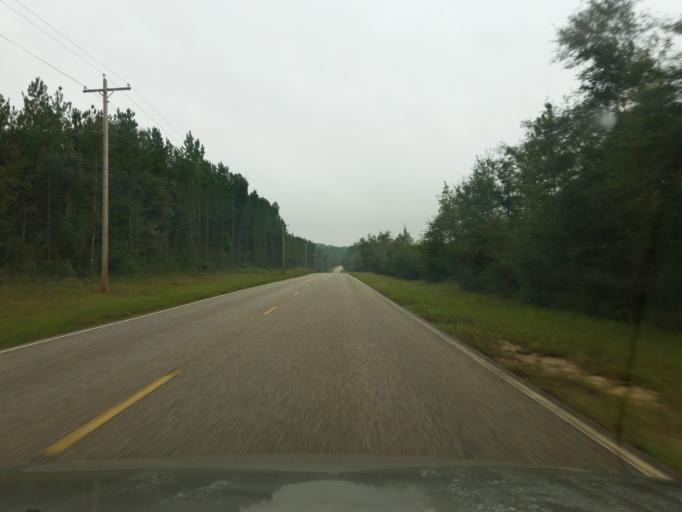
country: US
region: Florida
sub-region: Escambia County
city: Cantonment
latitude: 30.6239
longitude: -87.4293
